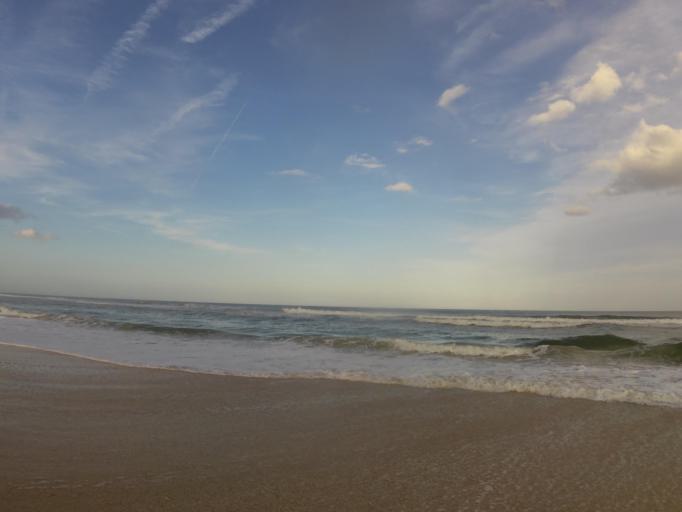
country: US
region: Florida
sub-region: Flagler County
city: Palm Coast
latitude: 29.6302
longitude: -81.1964
